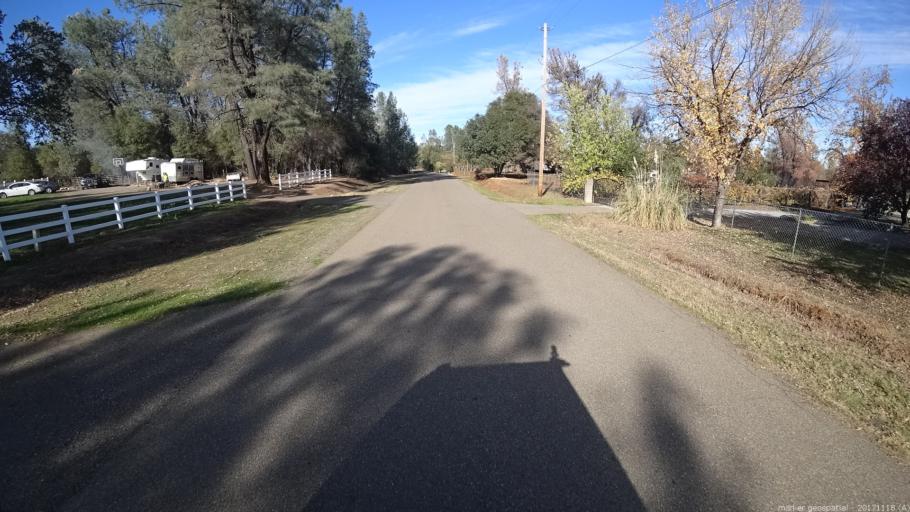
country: US
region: California
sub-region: Shasta County
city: Redding
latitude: 40.4785
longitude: -122.4381
